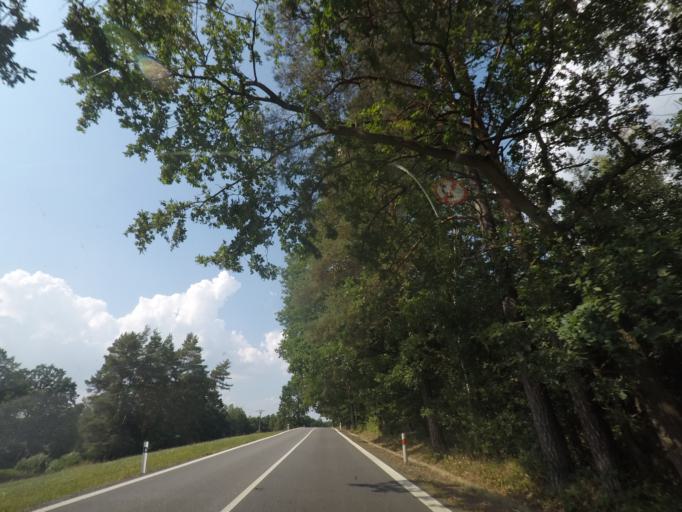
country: CZ
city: Borohradek
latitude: 50.0773
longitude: 16.0732
